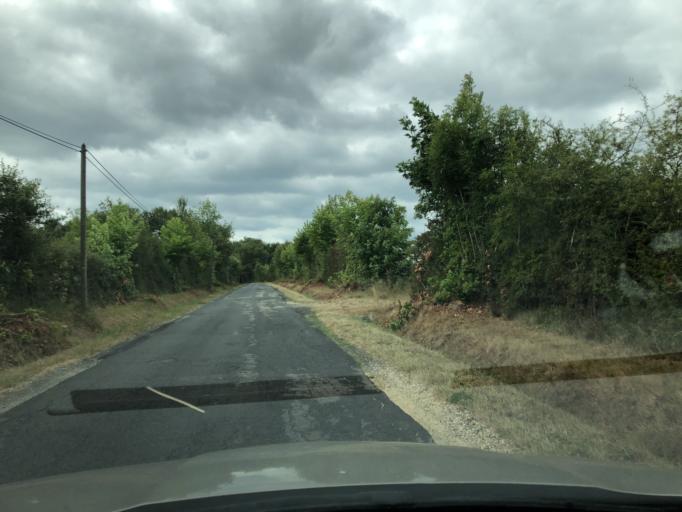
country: FR
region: Centre
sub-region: Departement d'Indre-et-Loire
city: Mazieres-de-Touraine
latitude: 47.3865
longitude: 0.4391
